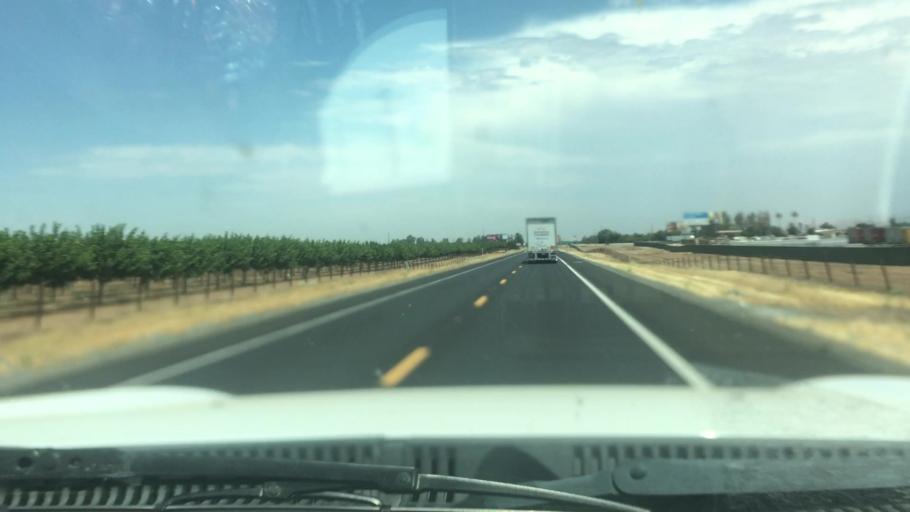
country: US
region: California
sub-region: Tulare County
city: Terra Bella
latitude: 35.9569
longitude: -119.0537
